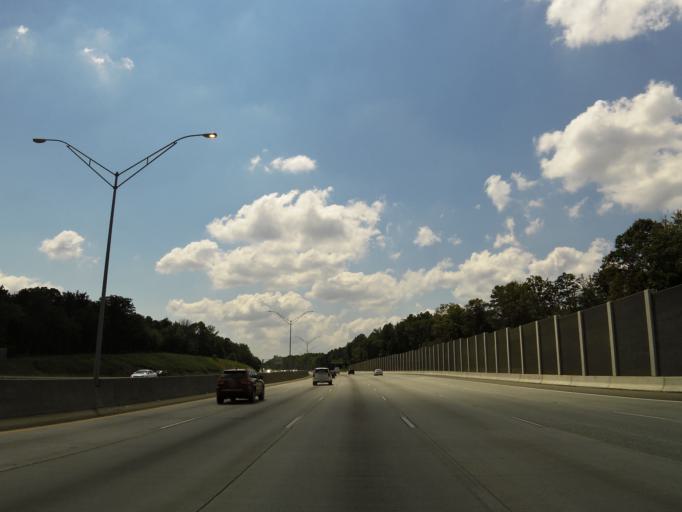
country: US
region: North Carolina
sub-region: Cabarrus County
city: Harrisburg
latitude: 35.3434
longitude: -80.7383
